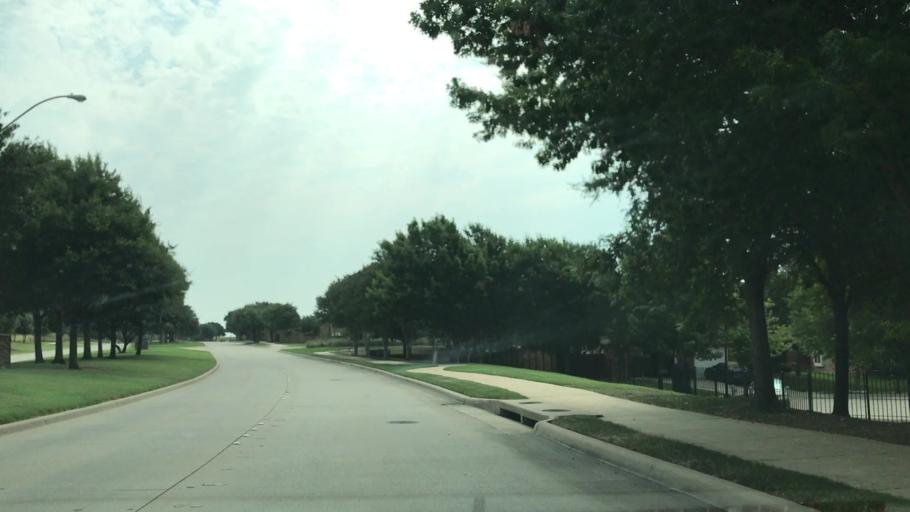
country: US
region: Texas
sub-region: Tarrant County
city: Keller
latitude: 32.9101
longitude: -97.2779
